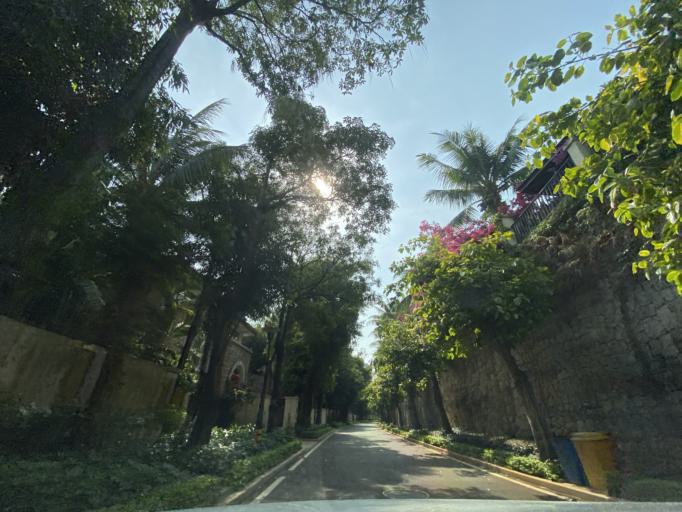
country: CN
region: Hainan
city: Yingzhou
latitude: 18.4092
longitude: 109.8456
